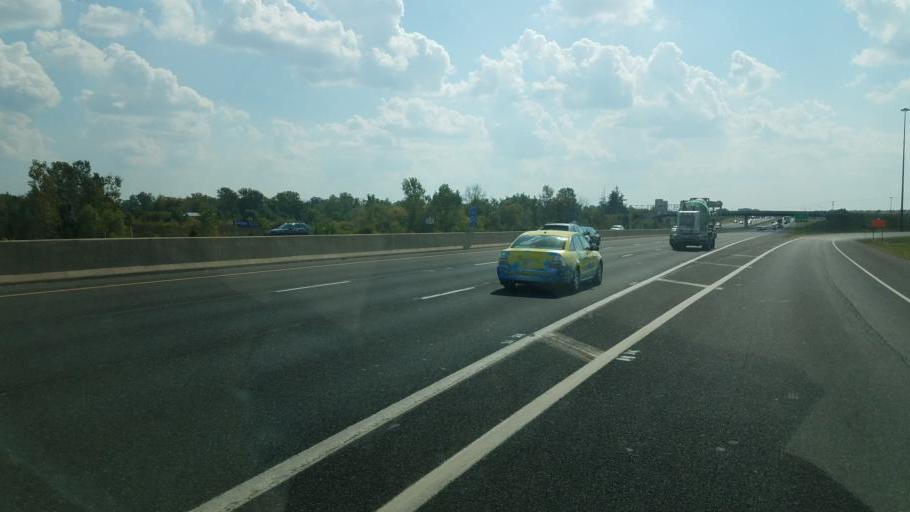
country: US
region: Indiana
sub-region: Allen County
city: Fort Wayne
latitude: 41.1675
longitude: -85.1049
